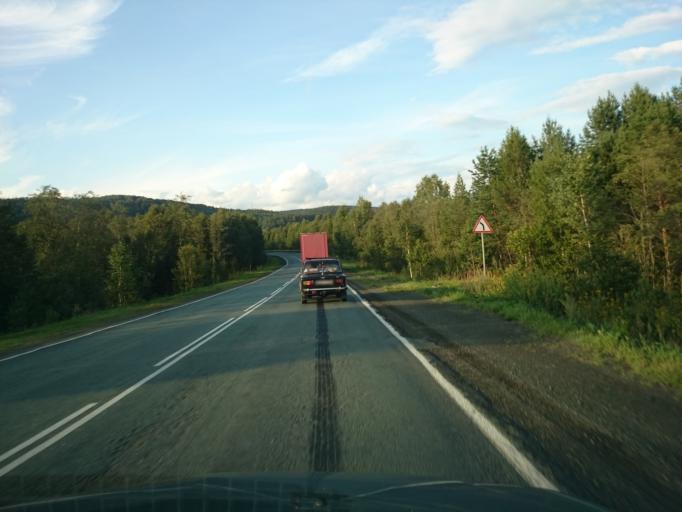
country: RU
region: Bashkortostan
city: Inzer
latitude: 53.9665
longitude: 57.8740
